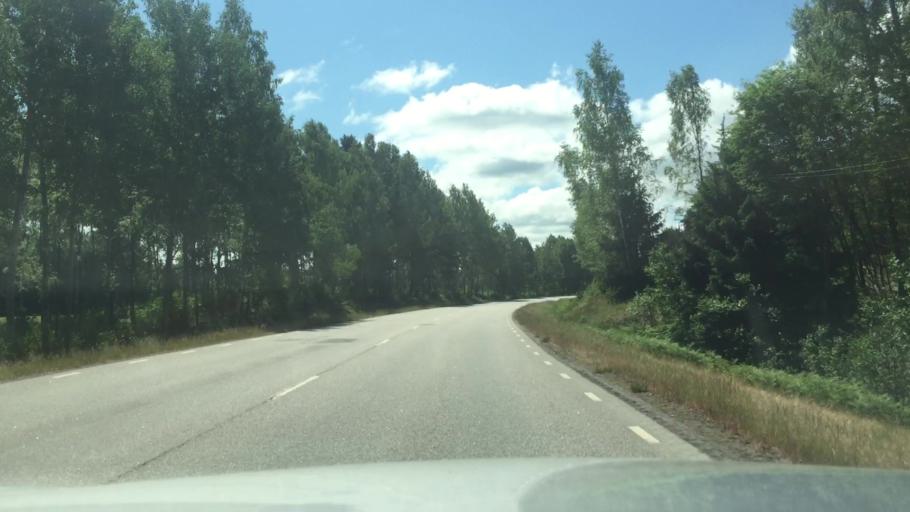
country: SE
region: Vaestra Goetaland
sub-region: Karlsborgs Kommun
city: Molltorp
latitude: 58.6264
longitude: 14.3888
